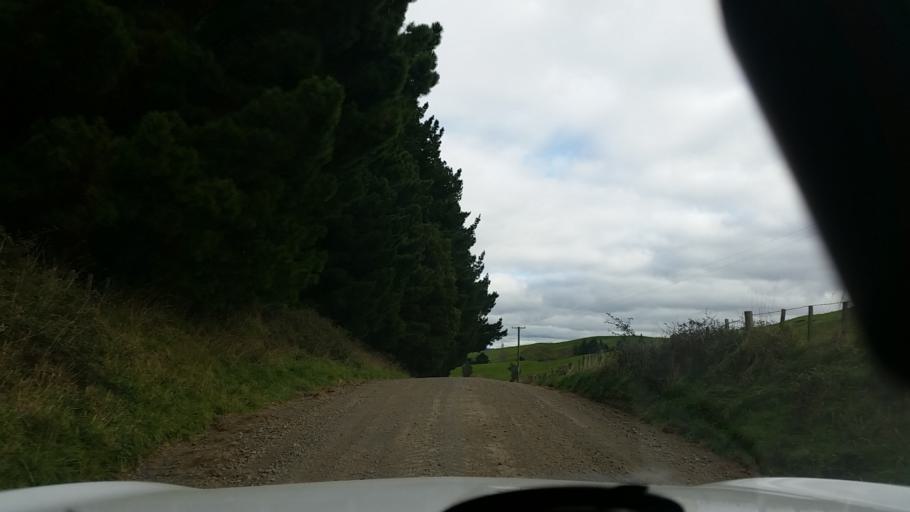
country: NZ
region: Hawke's Bay
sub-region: Napier City
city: Napier
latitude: -39.1809
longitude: 176.8547
